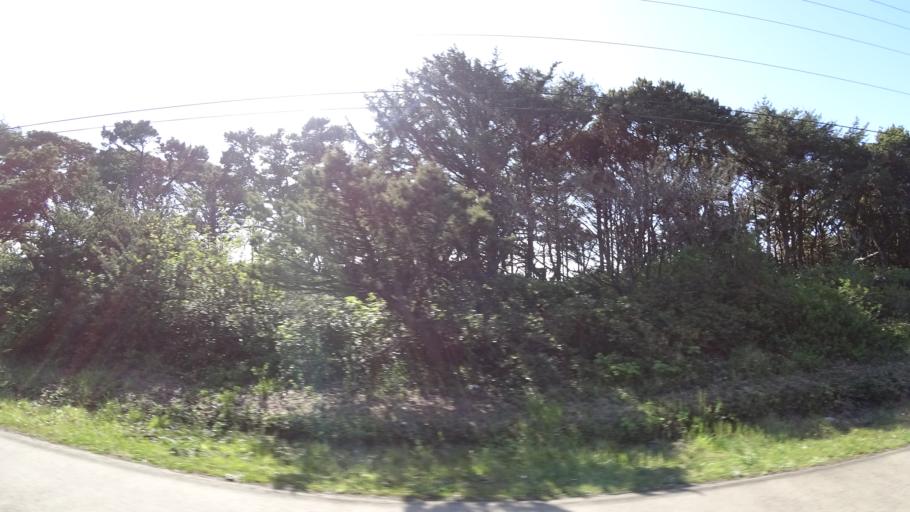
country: US
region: Oregon
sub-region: Lincoln County
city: Newport
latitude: 44.5517
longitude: -124.0722
